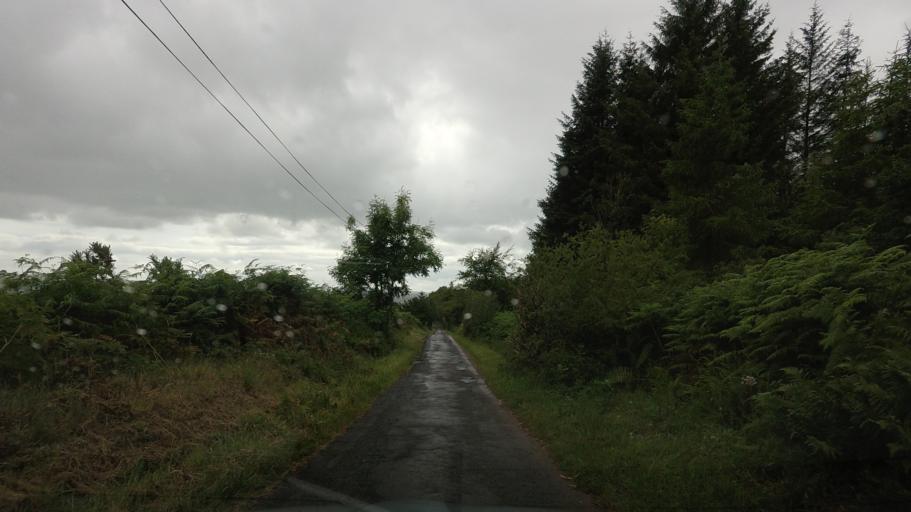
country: GB
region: Scotland
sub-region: Stirling
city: Killearn
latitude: 56.0838
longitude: -4.4453
